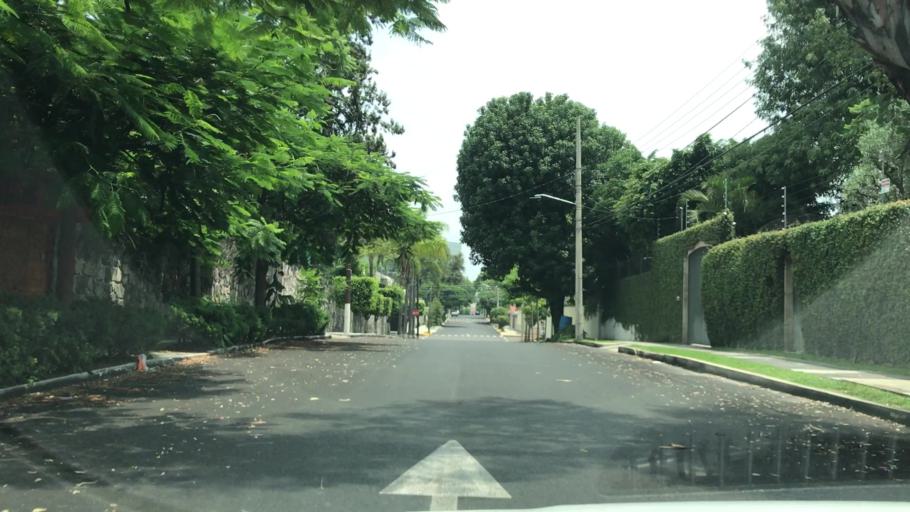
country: MX
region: Jalisco
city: Guadalajara
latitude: 20.6556
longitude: -103.4049
